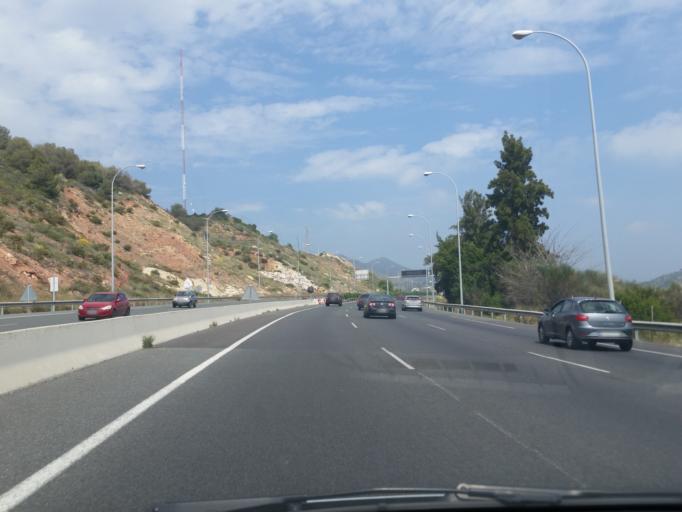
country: ES
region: Andalusia
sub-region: Provincia de Malaga
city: Malaga
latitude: 36.7295
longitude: -4.4542
